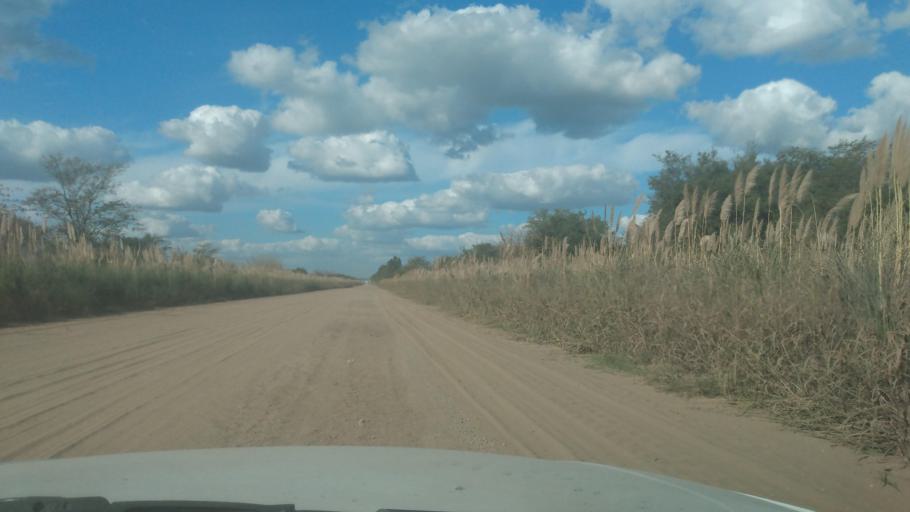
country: AR
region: Buenos Aires
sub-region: Partido de Navarro
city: Navarro
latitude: -35.0006
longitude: -59.3460
